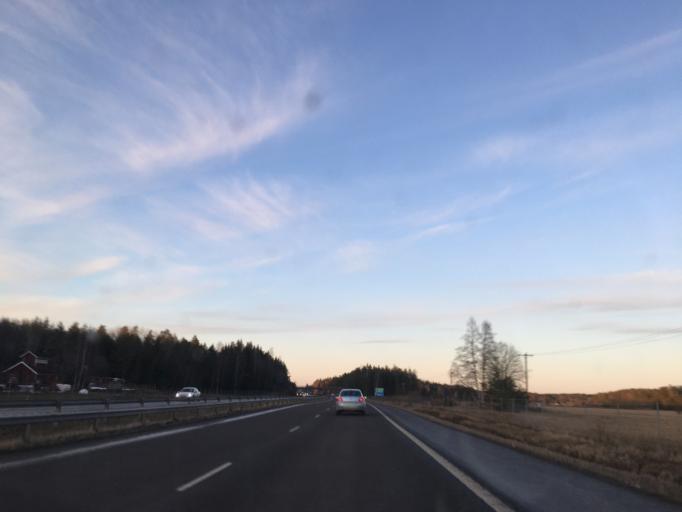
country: FI
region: Varsinais-Suomi
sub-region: Turku
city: Turku
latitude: 60.5213
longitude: 22.3048
